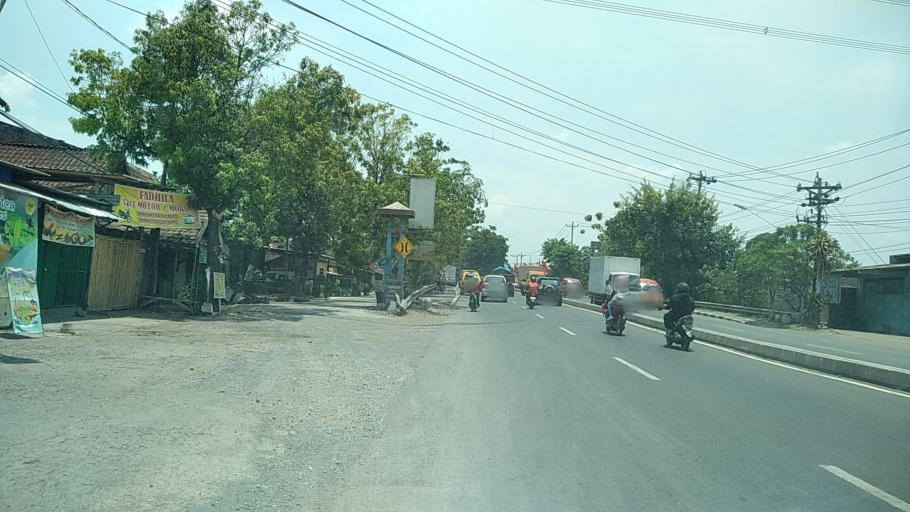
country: ID
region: Central Java
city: Mranggen
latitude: -7.0171
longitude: 110.4873
